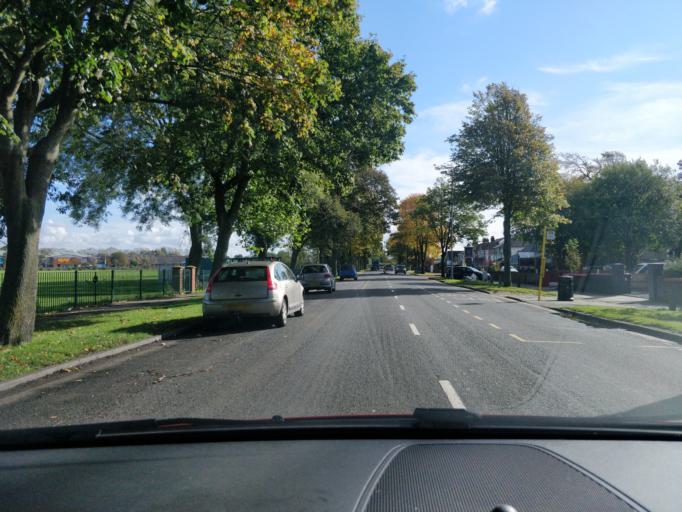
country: GB
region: England
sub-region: Sefton
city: Southport
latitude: 53.6347
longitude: -2.9748
